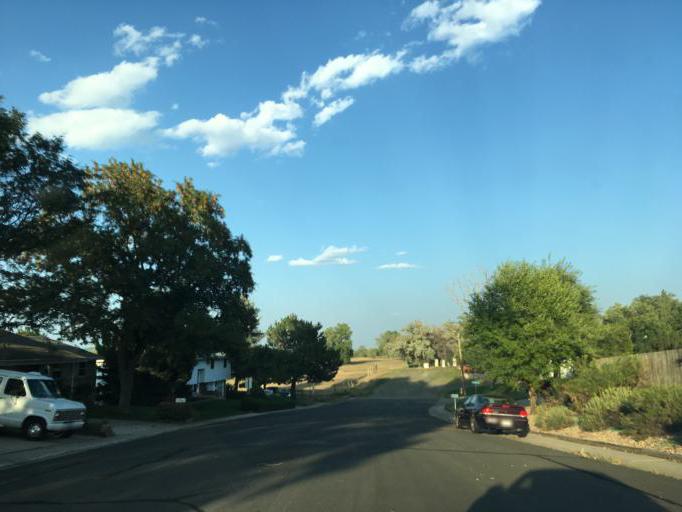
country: US
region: Colorado
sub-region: Jefferson County
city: Applewood
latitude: 39.7944
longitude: -105.1485
